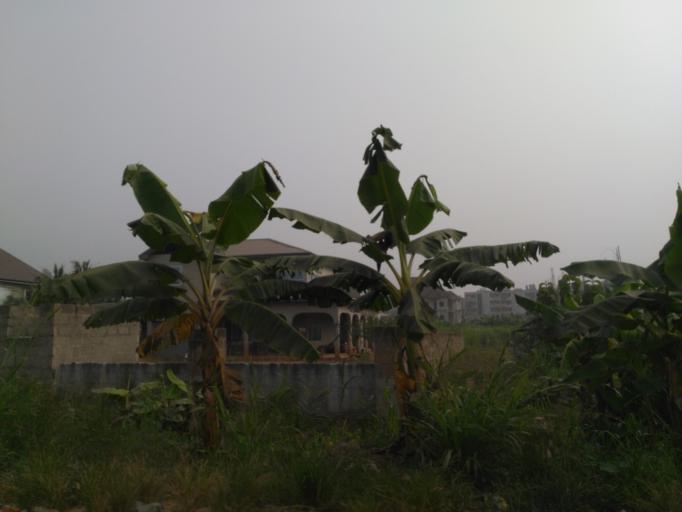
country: GH
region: Ashanti
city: Kumasi
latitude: 6.6566
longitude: -1.6262
